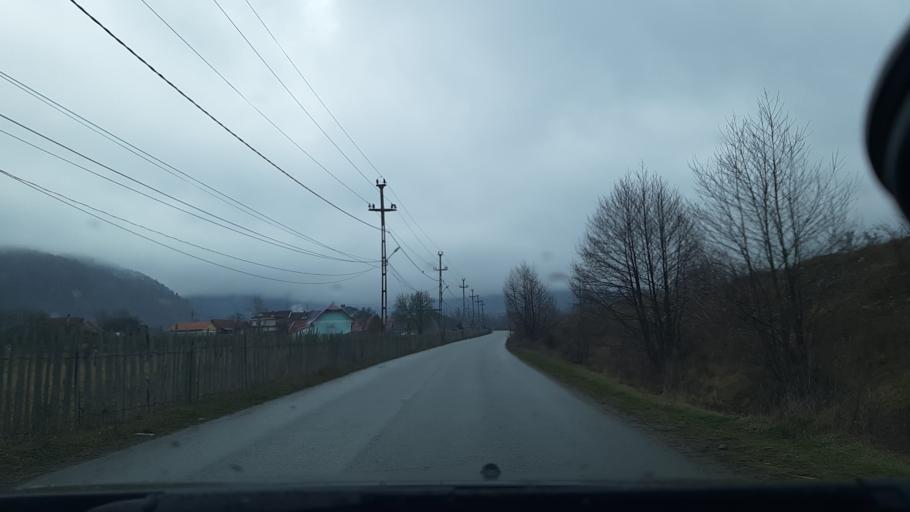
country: RO
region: Hunedoara
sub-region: Oras Petrila
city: Petrila
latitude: 45.4331
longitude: 23.4195
